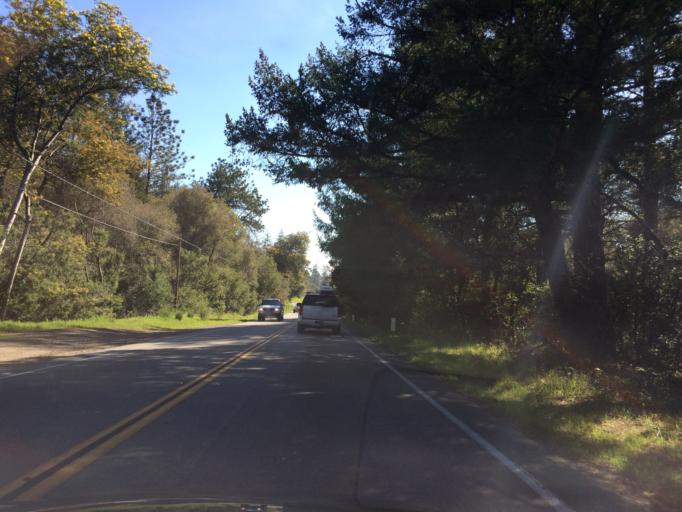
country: US
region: California
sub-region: Santa Cruz County
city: Pasatiempo
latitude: 37.0276
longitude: -122.0391
